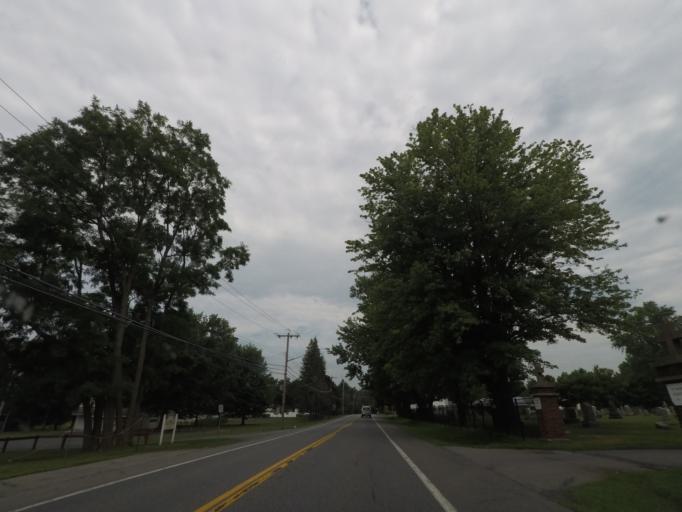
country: US
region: New York
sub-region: Saratoga County
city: Waterford
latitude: 42.8039
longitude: -73.6835
